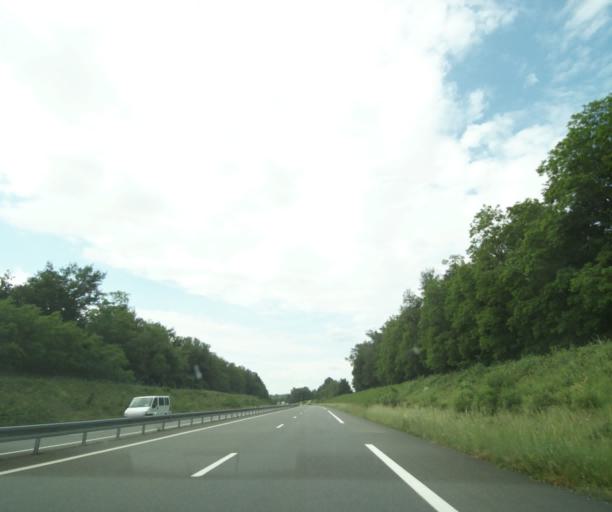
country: FR
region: Pays de la Loire
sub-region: Departement de Maine-et-Loire
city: Brion
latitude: 47.4477
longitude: -0.1768
